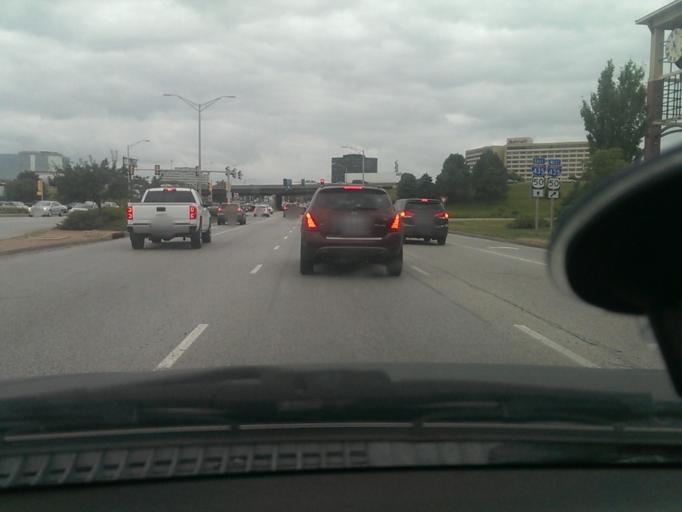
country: US
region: Kansas
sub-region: Johnson County
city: Overland Park
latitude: 38.9339
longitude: -94.6677
